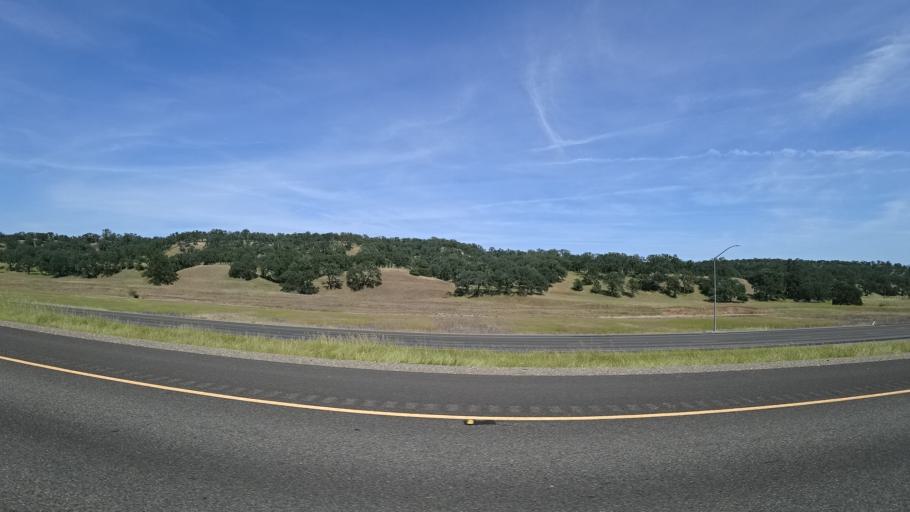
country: US
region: California
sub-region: Tehama County
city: Red Bluff
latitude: 40.2406
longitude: -122.2582
